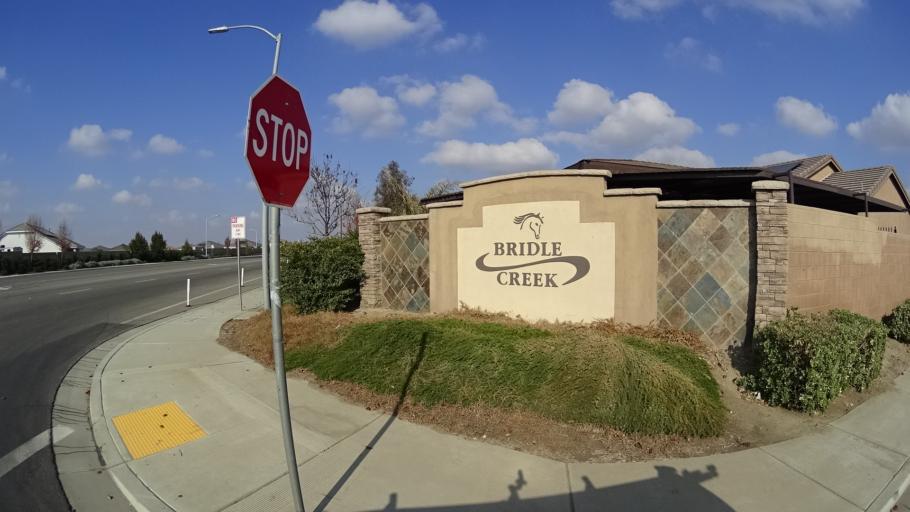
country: US
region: California
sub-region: Kern County
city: Greenacres
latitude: 35.2917
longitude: -119.1097
